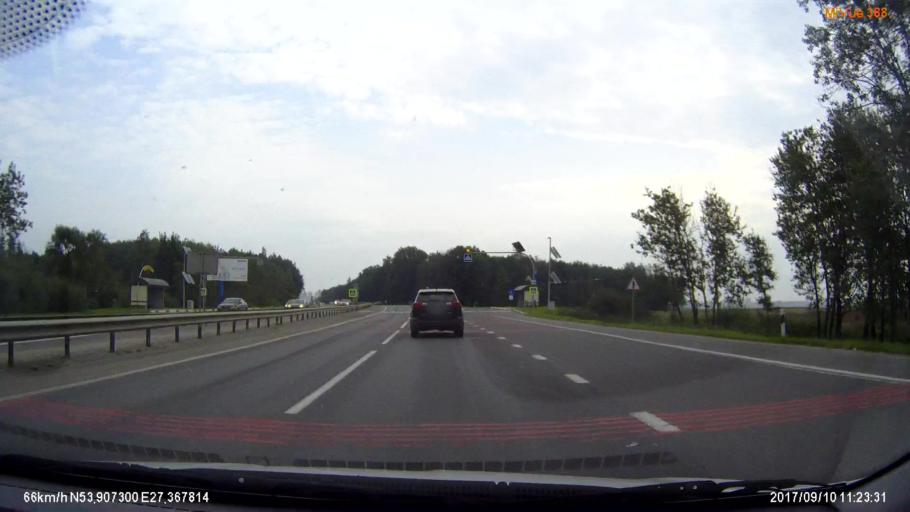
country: BY
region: Minsk
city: Khatsyezhyna
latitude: 53.9073
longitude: 27.3684
